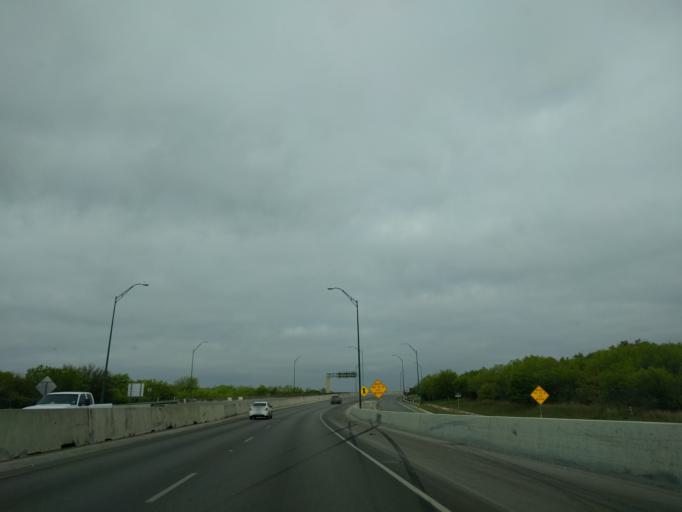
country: US
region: Texas
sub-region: Bexar County
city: Windcrest
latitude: 29.5418
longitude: -98.4235
